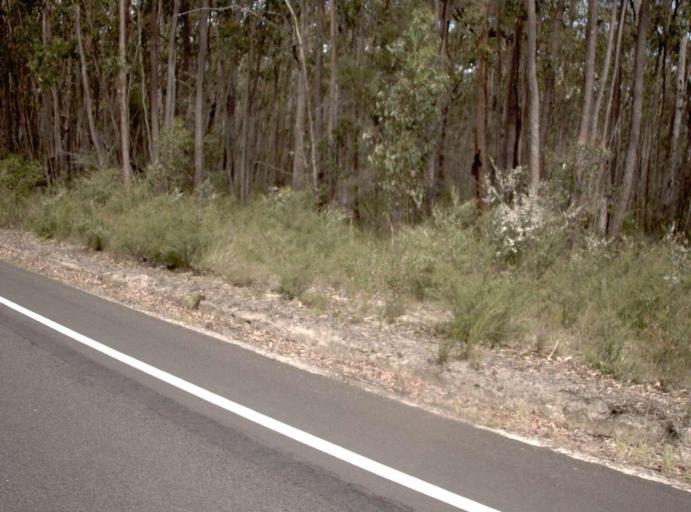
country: AU
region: New South Wales
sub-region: Bega Valley
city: Eden
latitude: -37.5080
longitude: 149.5239
